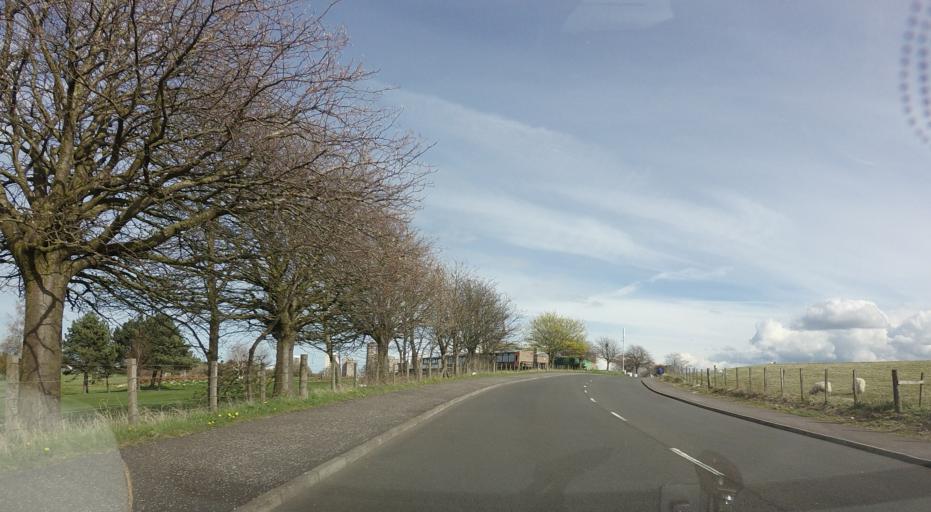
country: GB
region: Scotland
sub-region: Edinburgh
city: Colinton
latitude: 55.9734
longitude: -3.2746
